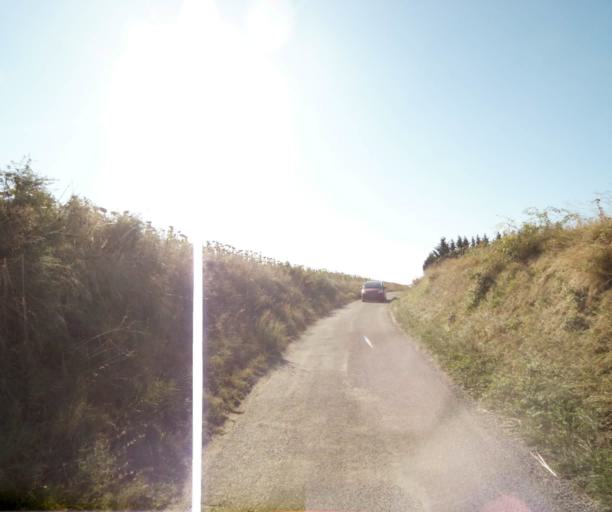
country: FR
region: Midi-Pyrenees
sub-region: Departement du Tarn-et-Garonne
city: Verdun-sur-Garonne
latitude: 43.8622
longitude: 1.2251
